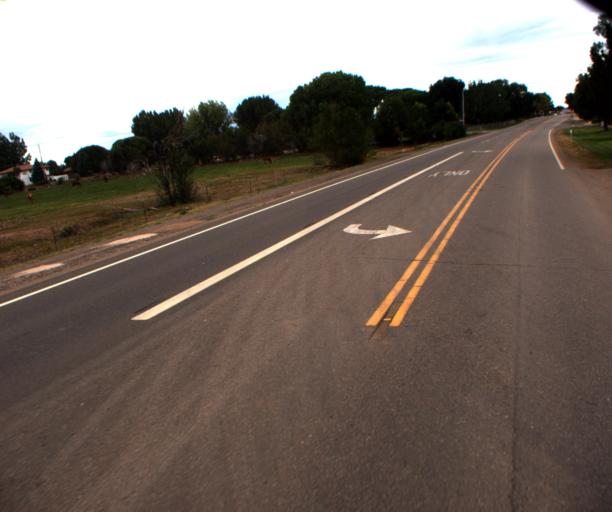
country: US
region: Arizona
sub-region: Navajo County
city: Snowflake
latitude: 34.5183
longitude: -110.0790
